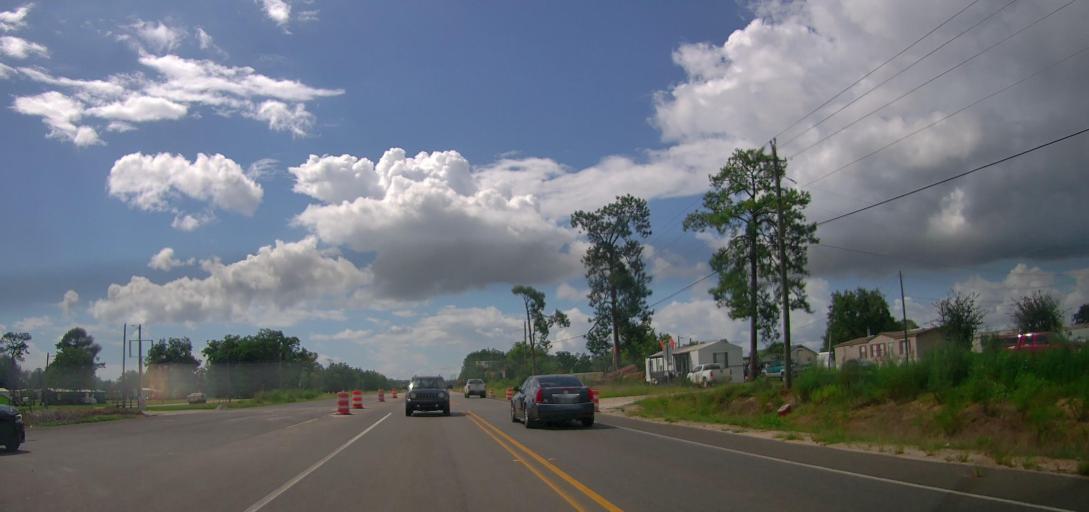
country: US
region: Georgia
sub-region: Coffee County
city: Douglas
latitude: 31.5374
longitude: -82.9214
